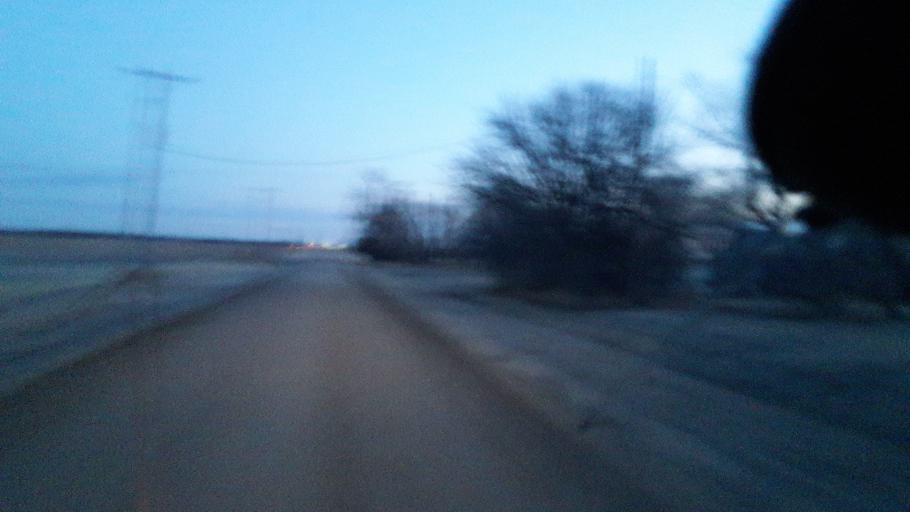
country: US
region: Kansas
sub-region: Reno County
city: South Hutchinson
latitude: 38.0050
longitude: -97.9768
